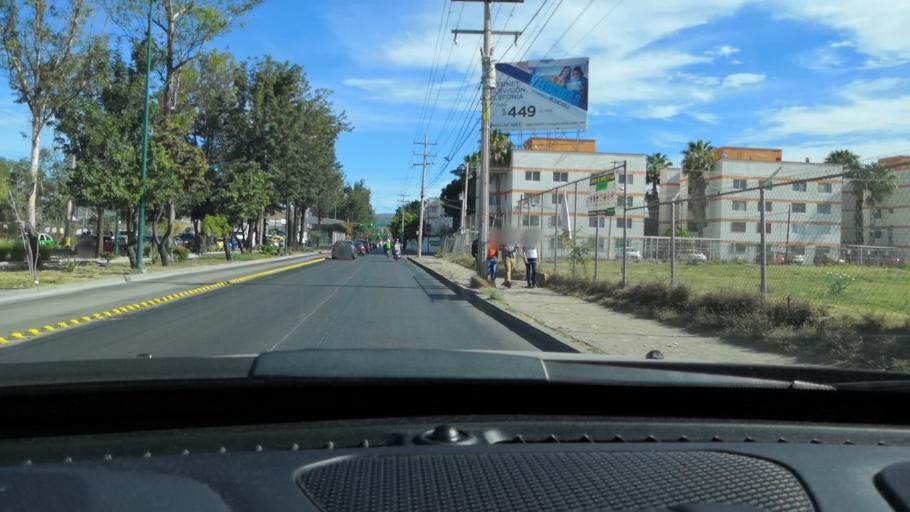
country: MX
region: Guanajuato
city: Leon
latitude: 21.1529
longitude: -101.6691
